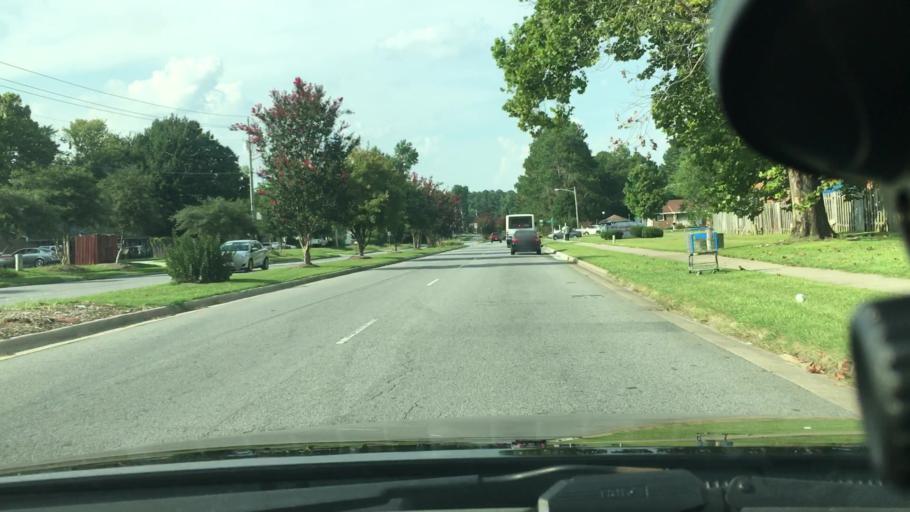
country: US
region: North Carolina
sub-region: Pitt County
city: Summerfield
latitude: 35.5793
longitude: -77.3900
